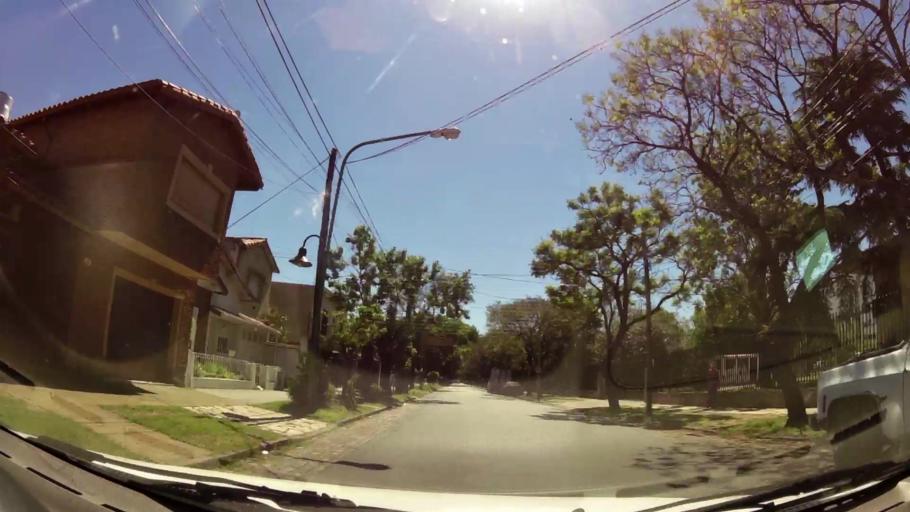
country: AR
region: Buenos Aires
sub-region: Partido de Vicente Lopez
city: Olivos
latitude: -34.5210
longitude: -58.5057
